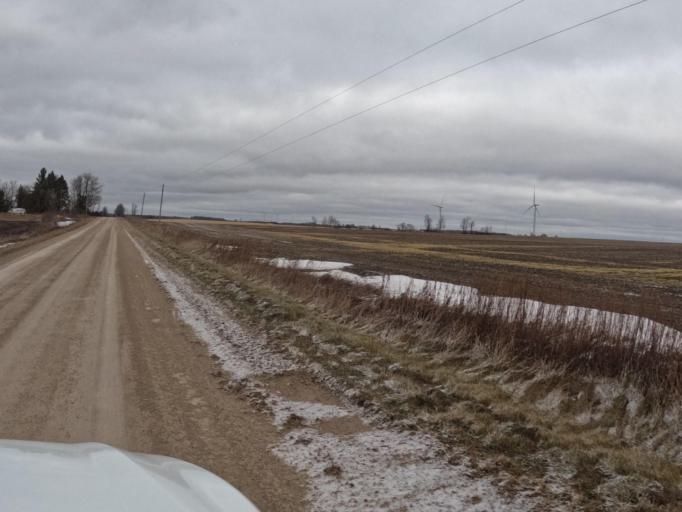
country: CA
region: Ontario
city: Shelburne
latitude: 44.0243
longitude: -80.3699
